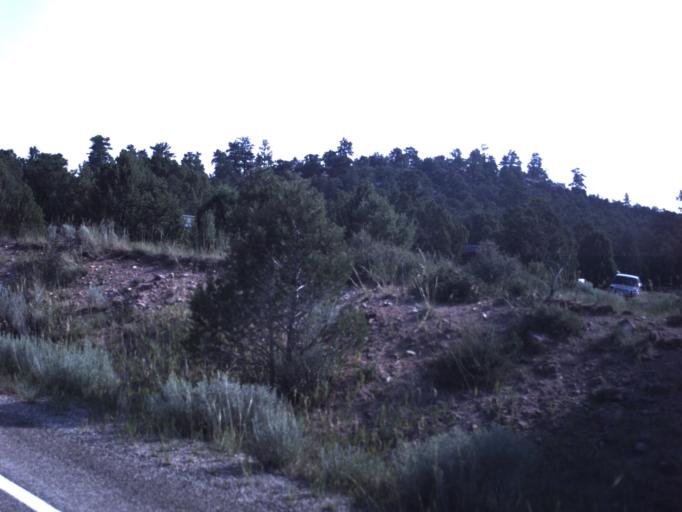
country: US
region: Utah
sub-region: Daggett County
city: Manila
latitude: 40.9126
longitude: -109.4117
